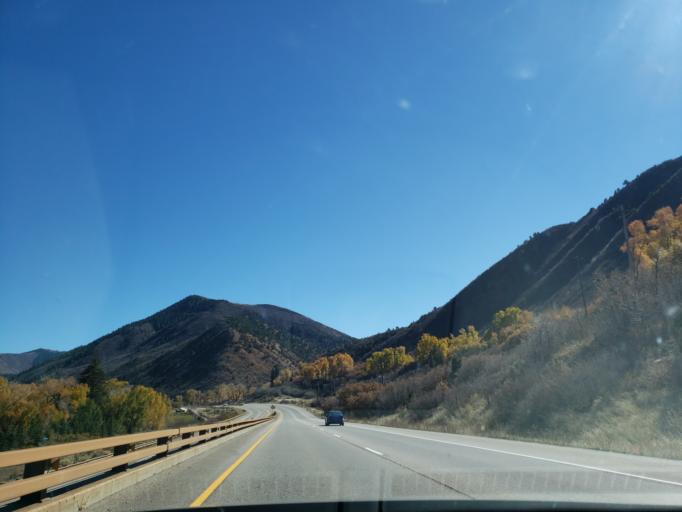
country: US
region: Colorado
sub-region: Eagle County
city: Basalt
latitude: 39.3341
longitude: -106.9921
